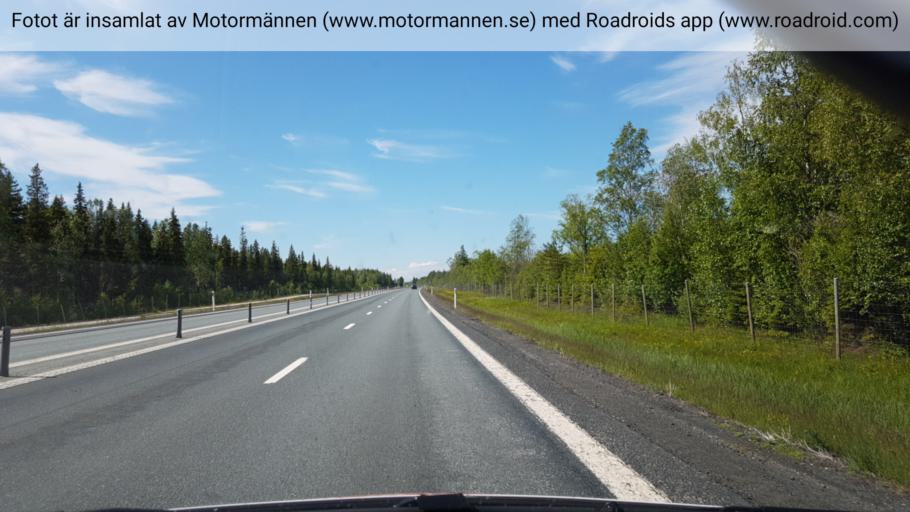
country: SE
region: Norrbotten
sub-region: Haparanda Kommun
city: Haparanda
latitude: 65.8095
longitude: 23.9702
